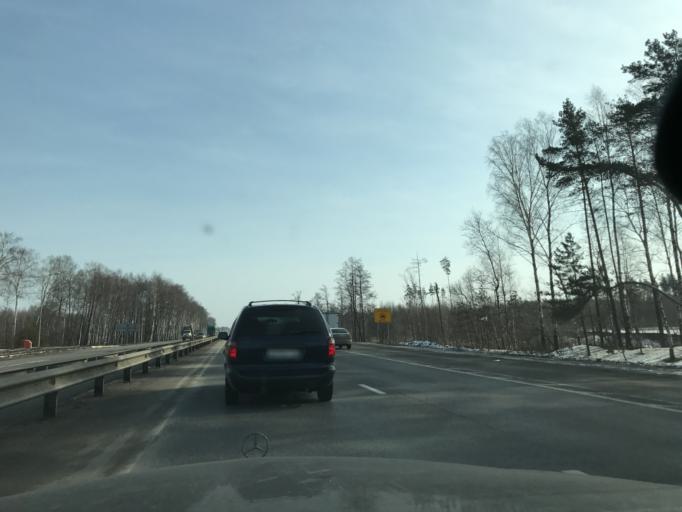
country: RU
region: Nizjnij Novgorod
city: Babino
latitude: 56.3031
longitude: 43.5915
